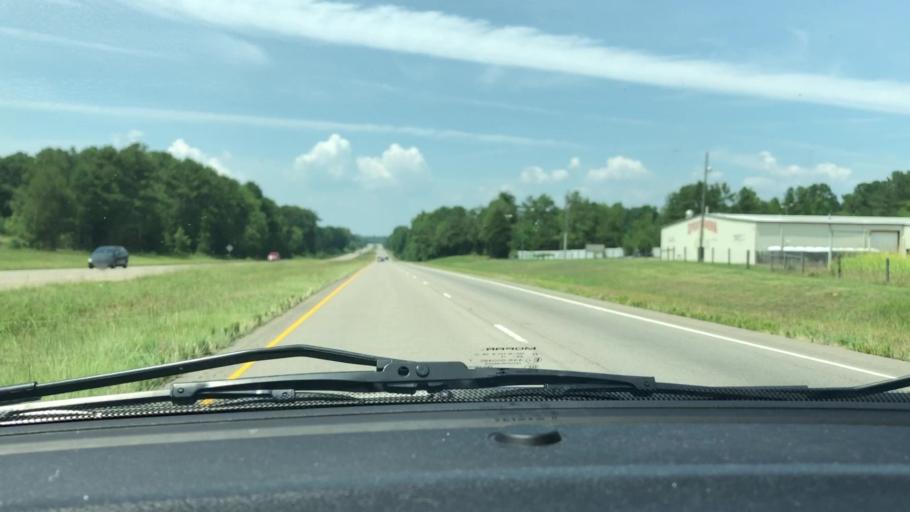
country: US
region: North Carolina
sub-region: Chatham County
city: Farmville
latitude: 35.5789
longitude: -79.3107
